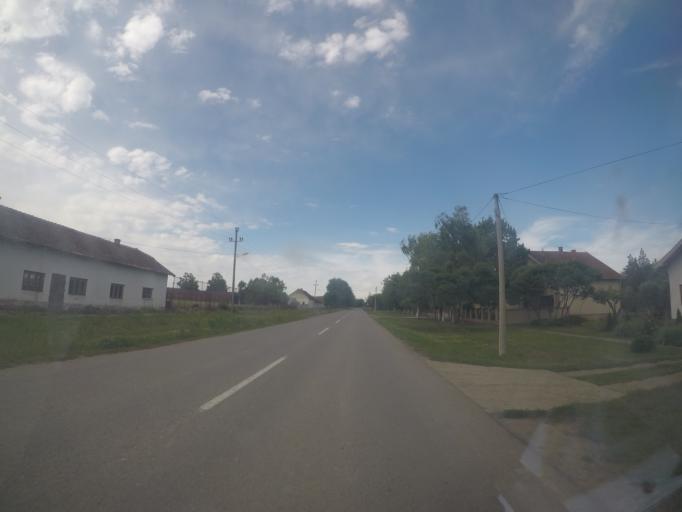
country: RS
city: Perlez
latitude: 45.2162
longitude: 20.3890
